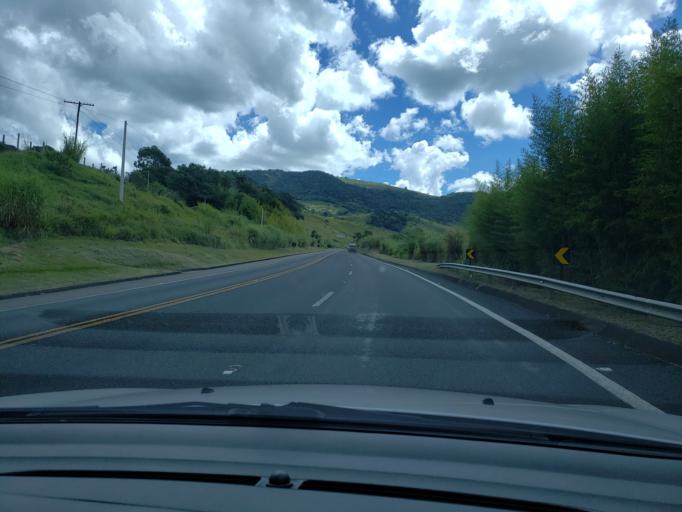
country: BR
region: Sao Paulo
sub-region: Sao Joao Da Boa Vista
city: Sao Joao da Boa Vista
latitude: -21.8945
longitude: -46.6962
